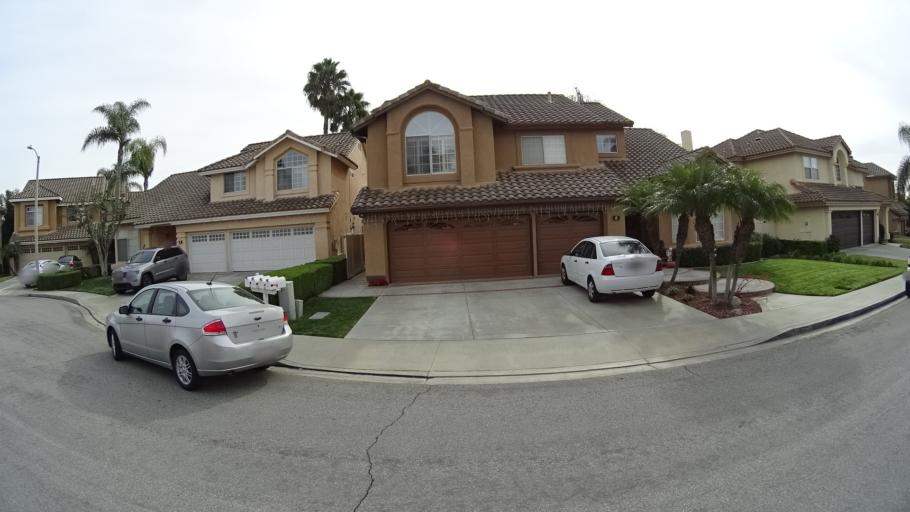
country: US
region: California
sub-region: Orange County
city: Laguna Woods
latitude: 33.5931
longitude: -117.7404
